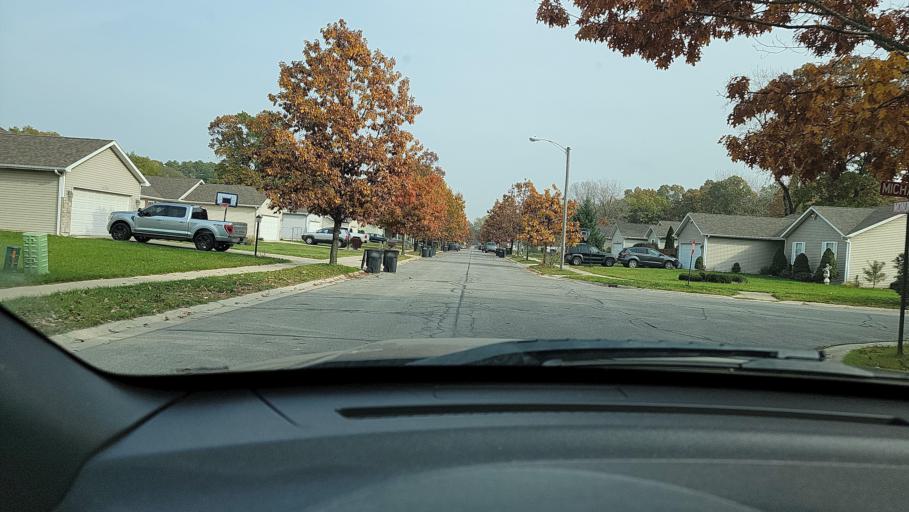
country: US
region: Indiana
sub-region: Porter County
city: Portage
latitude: 41.5904
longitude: -87.1684
